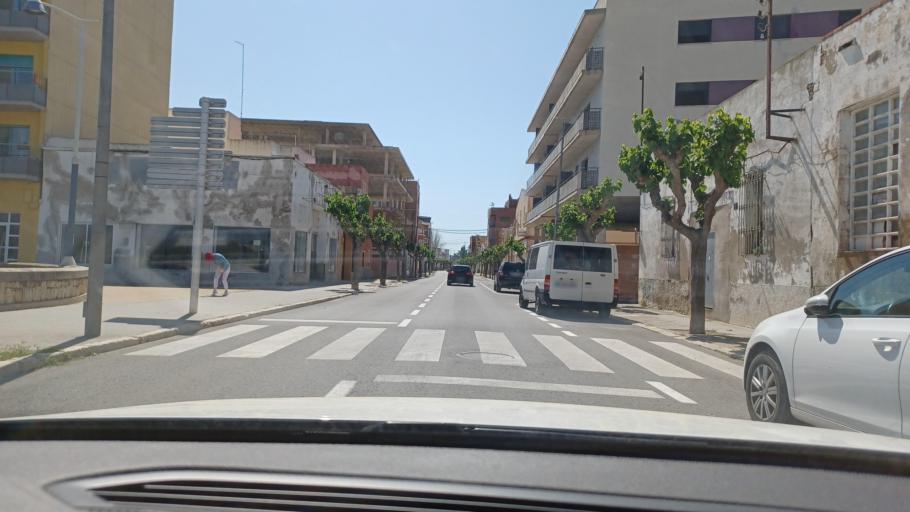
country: ES
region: Catalonia
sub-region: Provincia de Tarragona
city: Amposta
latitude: 40.7124
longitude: 0.5840
